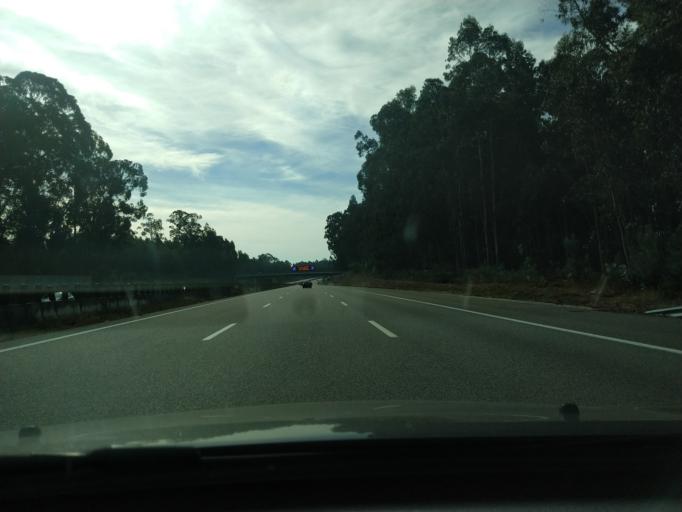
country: PT
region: Aveiro
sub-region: Estarreja
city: Avanca
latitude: 40.8219
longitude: -8.5521
